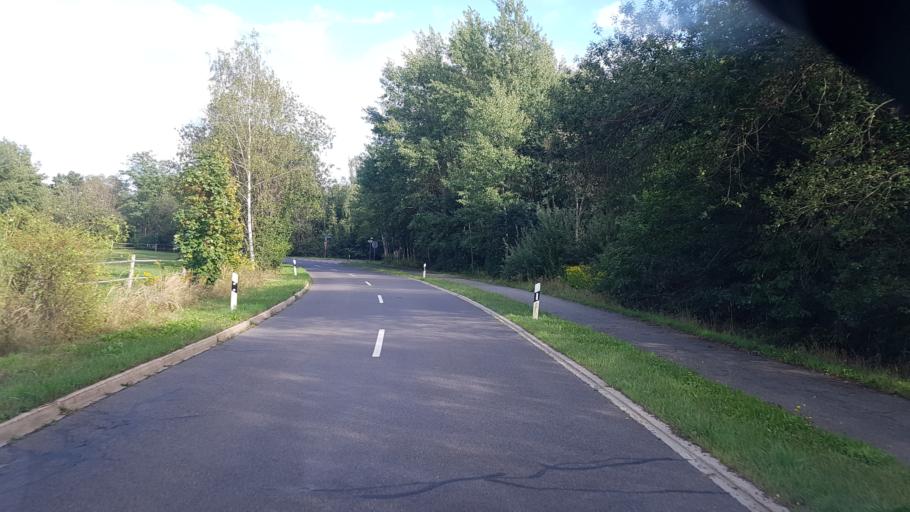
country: DE
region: Brandenburg
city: Spremberg
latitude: 51.5564
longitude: 14.3167
